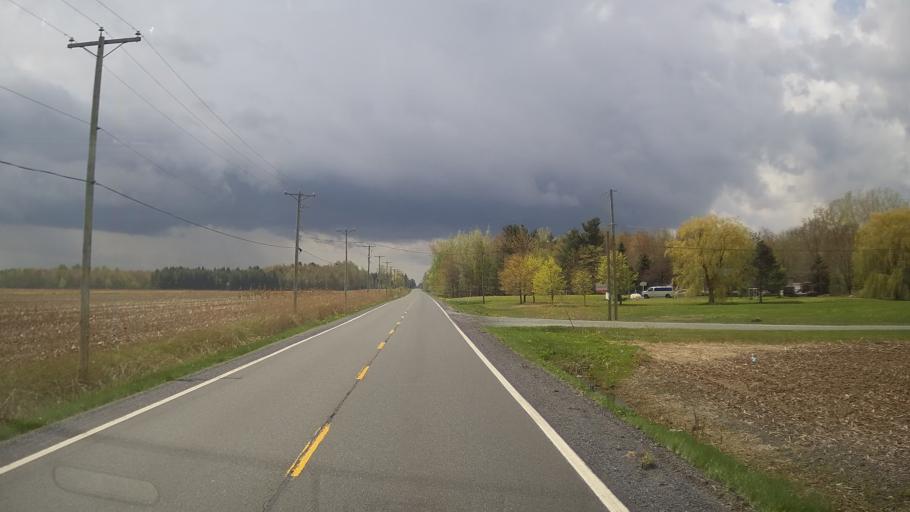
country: CA
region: Quebec
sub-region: Monteregie
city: Rougemont
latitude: 45.3451
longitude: -73.1061
